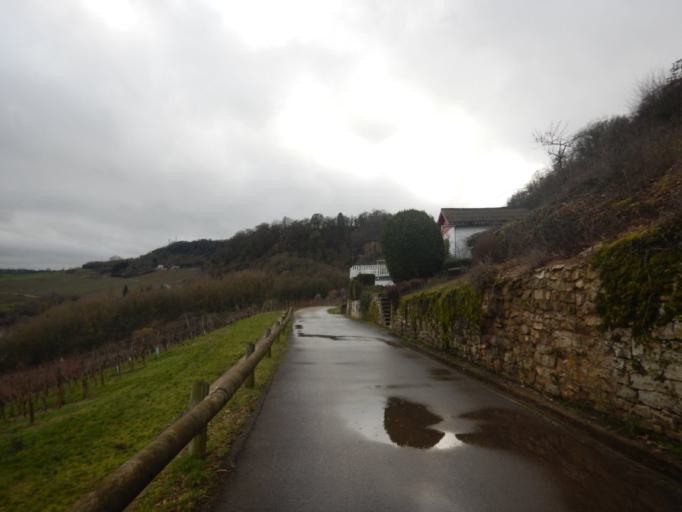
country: DE
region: Rheinland-Pfalz
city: Wellen
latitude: 49.6674
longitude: 6.4245
